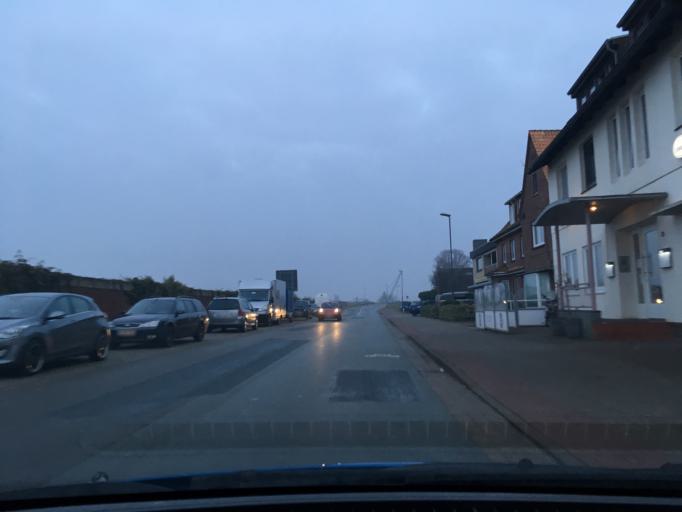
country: DE
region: Lower Saxony
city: Winsen
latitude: 53.3943
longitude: 10.1753
